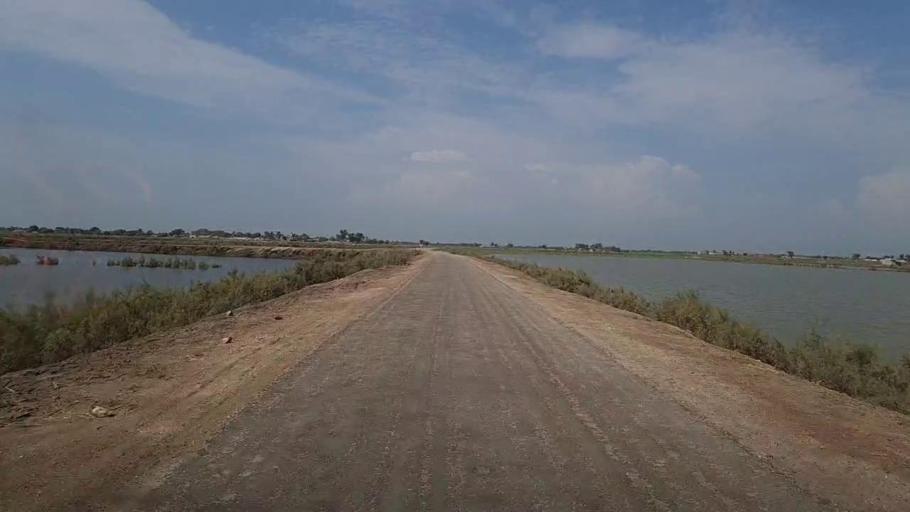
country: PK
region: Sindh
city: Thul
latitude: 28.2847
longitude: 68.8233
